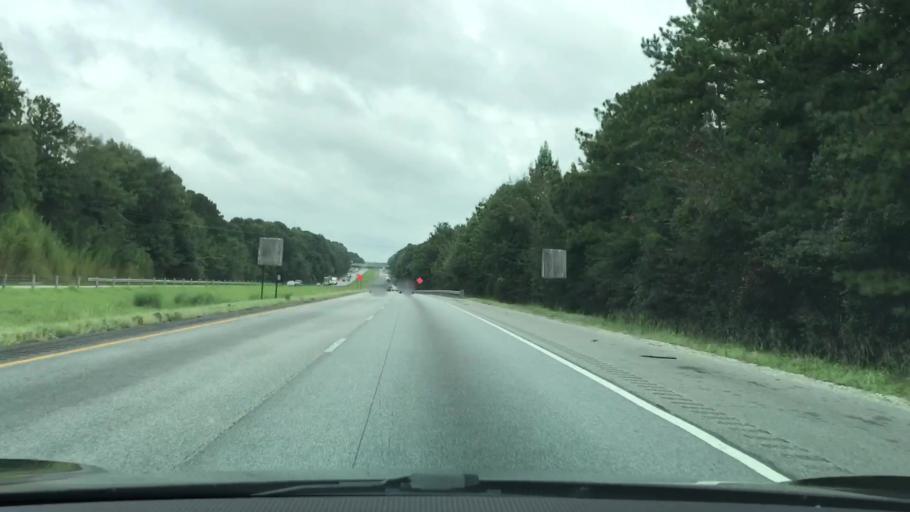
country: US
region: Alabama
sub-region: Lee County
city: Auburn
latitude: 32.5812
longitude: -85.4678
